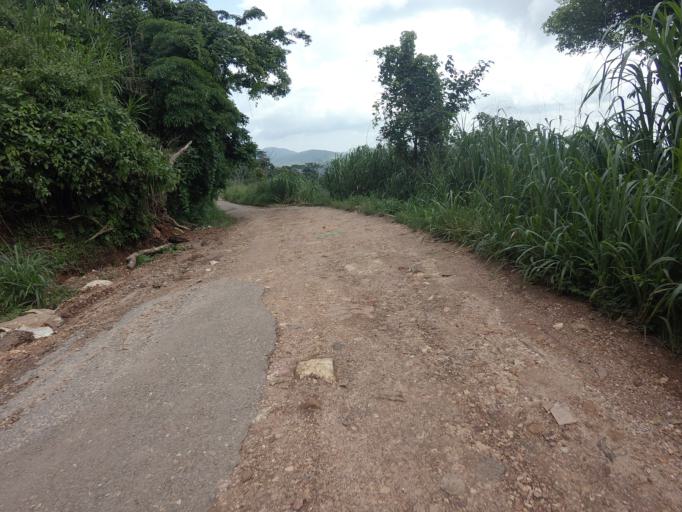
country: GH
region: Volta
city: Kpandu
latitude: 6.8396
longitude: 0.4292
